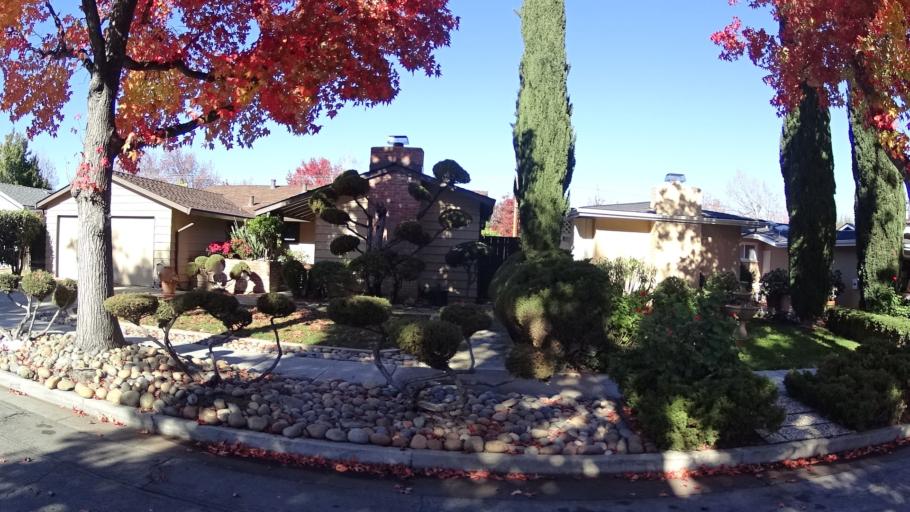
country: US
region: California
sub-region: Santa Clara County
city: Sunnyvale
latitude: 37.3584
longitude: -122.0119
